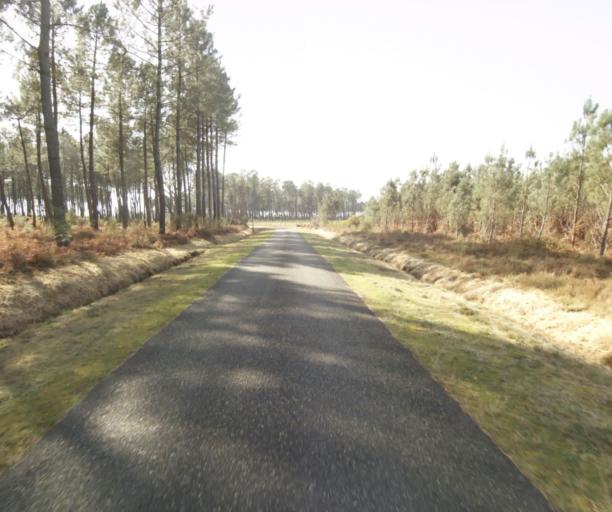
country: FR
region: Aquitaine
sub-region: Departement des Landes
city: Roquefort
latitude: 44.1467
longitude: -0.2630
